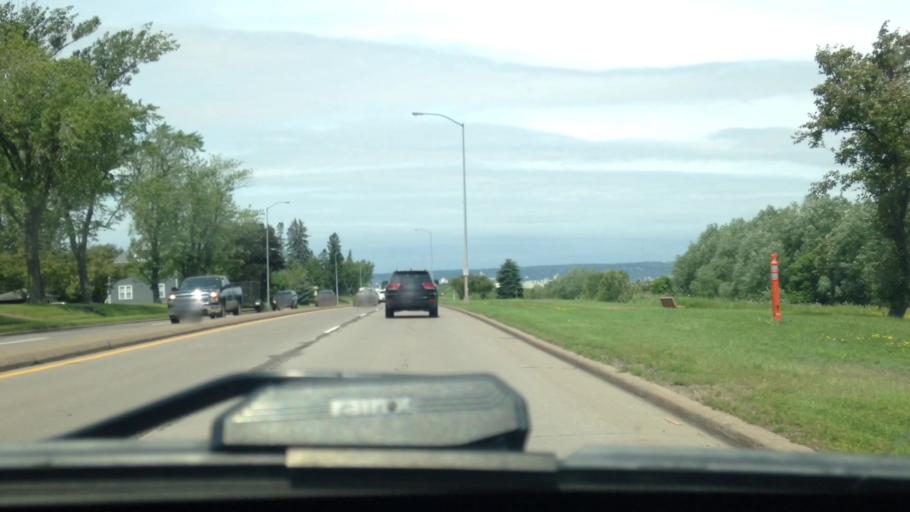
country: US
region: Wisconsin
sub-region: Douglas County
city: Superior
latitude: 46.7142
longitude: -92.0569
